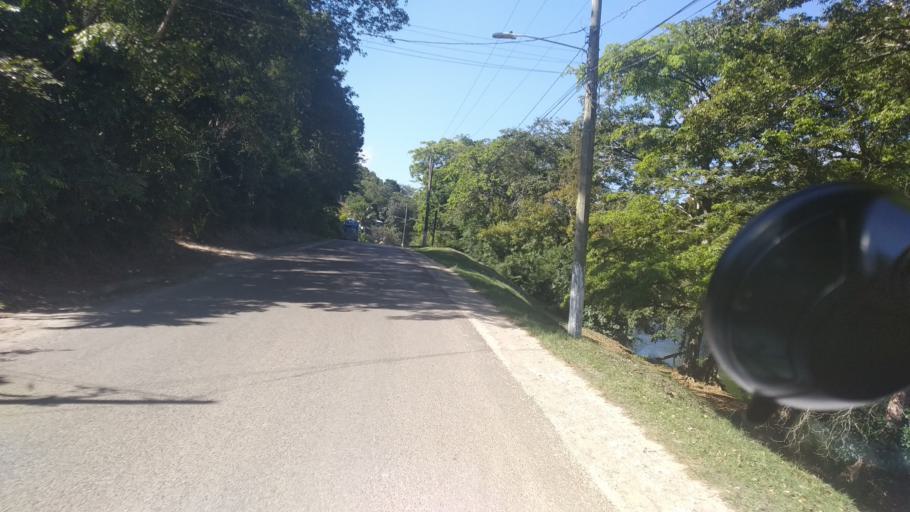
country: BZ
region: Cayo
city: Benque Viejo del Carmen
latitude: 17.0844
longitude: -89.1344
